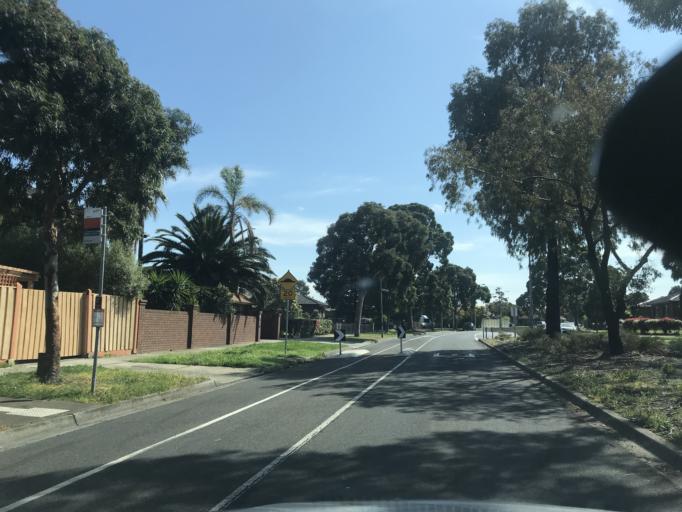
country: AU
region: Victoria
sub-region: Whittlesea
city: Epping
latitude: -37.6455
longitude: 145.0392
